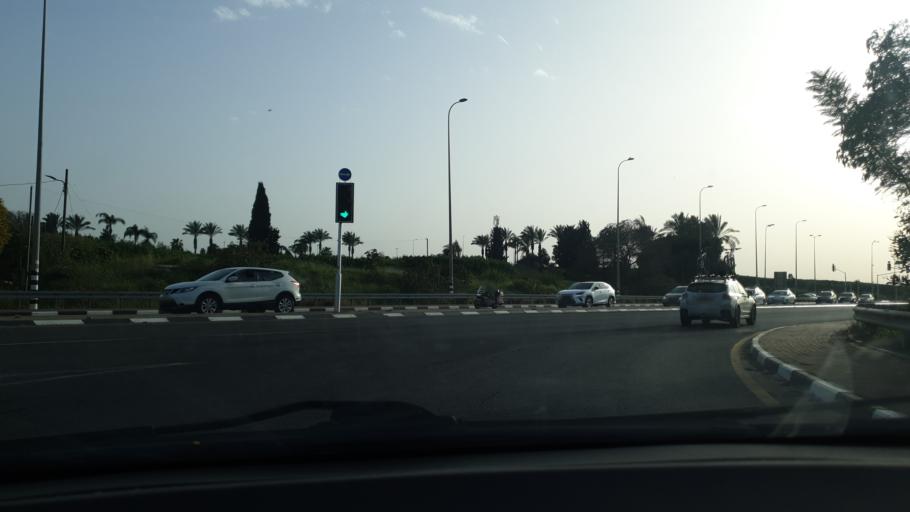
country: IL
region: Central District
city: Tel Mond
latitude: 32.2614
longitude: 34.9154
